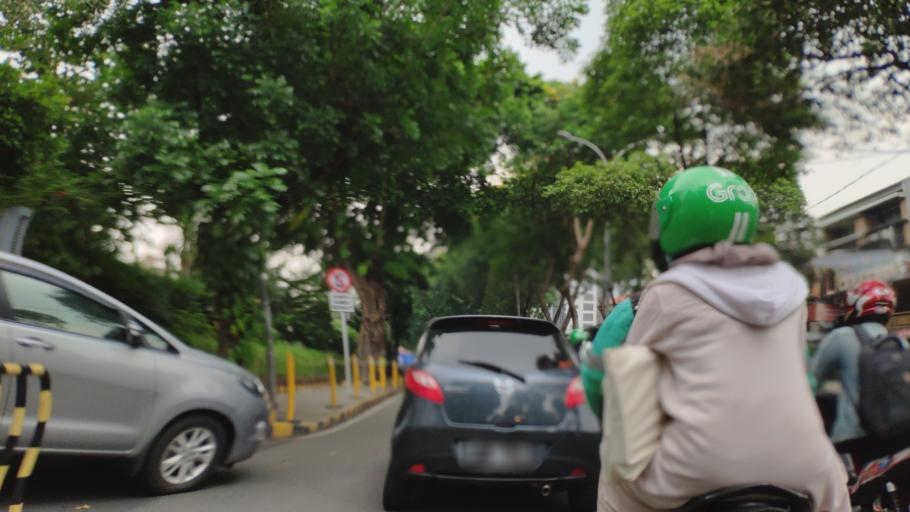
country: ID
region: Jakarta Raya
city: Jakarta
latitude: -6.2456
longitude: 106.7840
